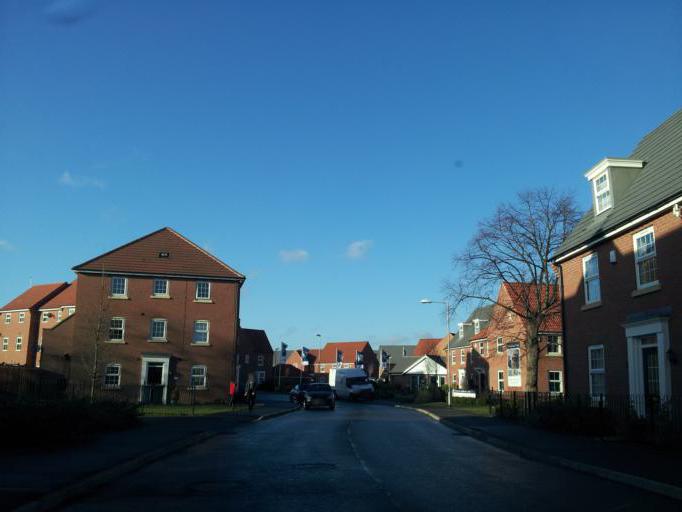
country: GB
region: England
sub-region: Nottinghamshire
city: Newark on Trent
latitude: 53.0470
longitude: -0.7660
